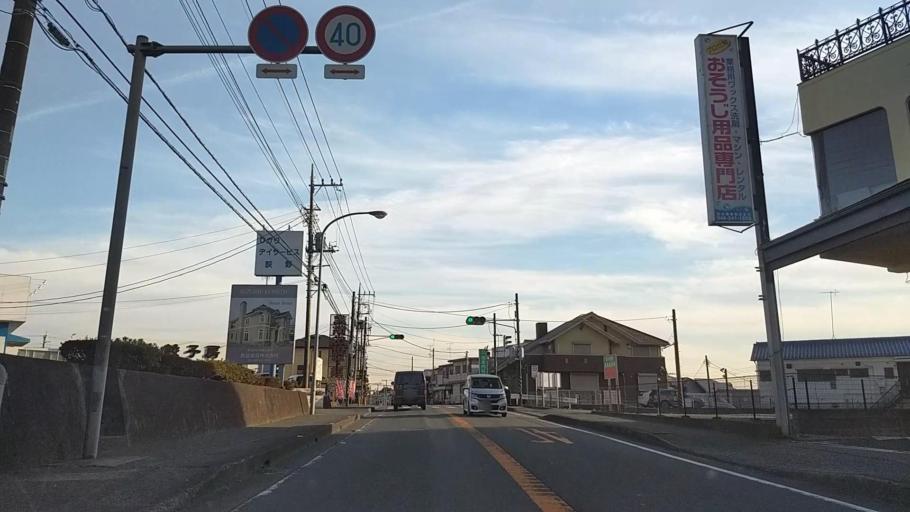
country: JP
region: Kanagawa
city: Atsugi
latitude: 35.4951
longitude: 139.3168
